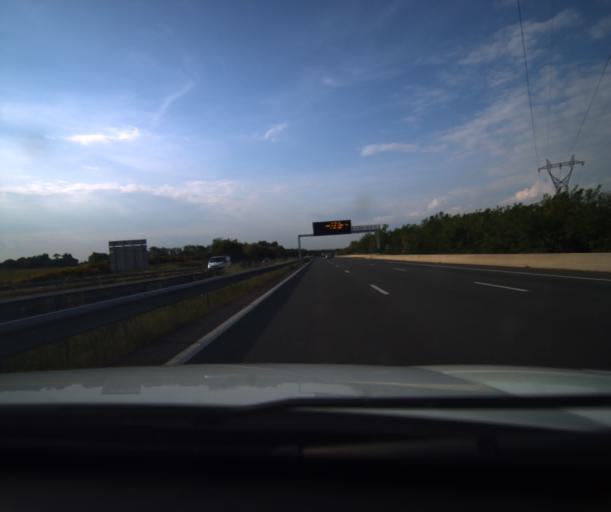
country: FR
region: Midi-Pyrenees
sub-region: Departement du Tarn-et-Garonne
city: Campsas
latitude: 43.8954
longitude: 1.3169
